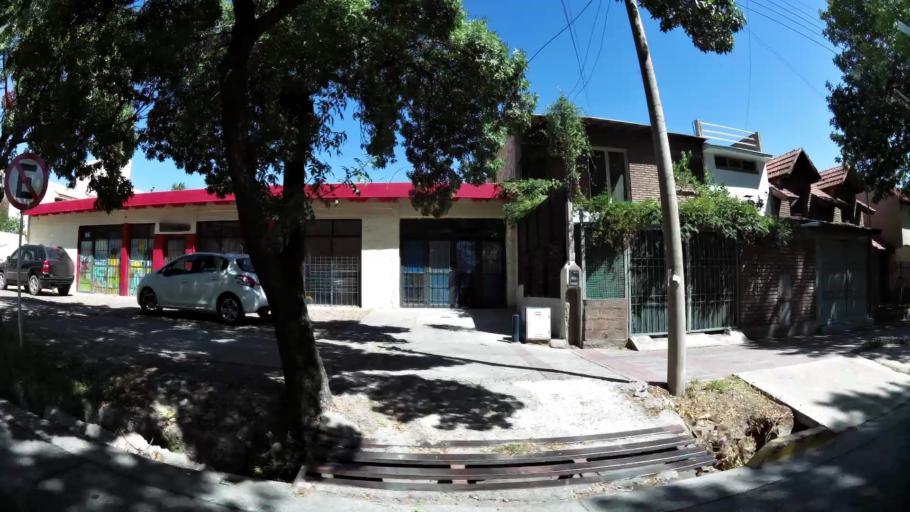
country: AR
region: Mendoza
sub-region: Departamento de Godoy Cruz
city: Godoy Cruz
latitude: -32.9399
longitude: -68.8581
